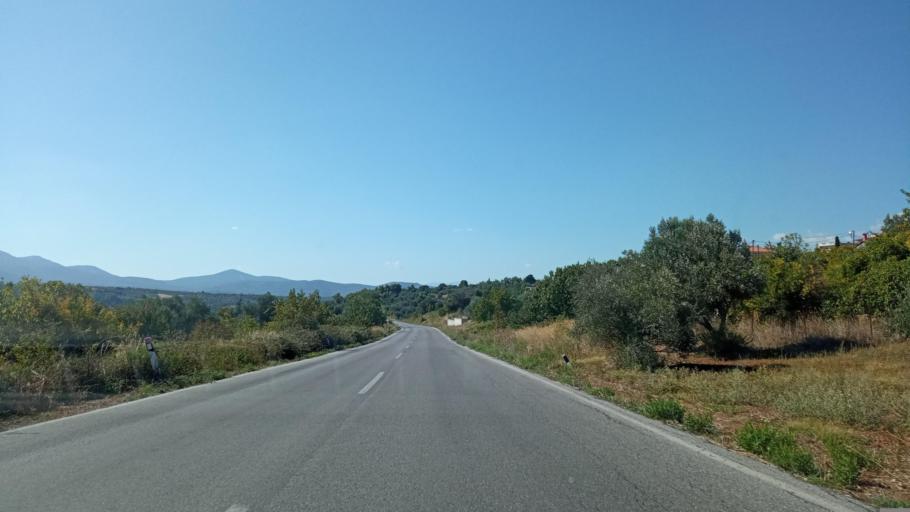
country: GR
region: Central Greece
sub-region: Nomos Evvoias
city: Kastella
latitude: 38.5732
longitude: 23.7757
